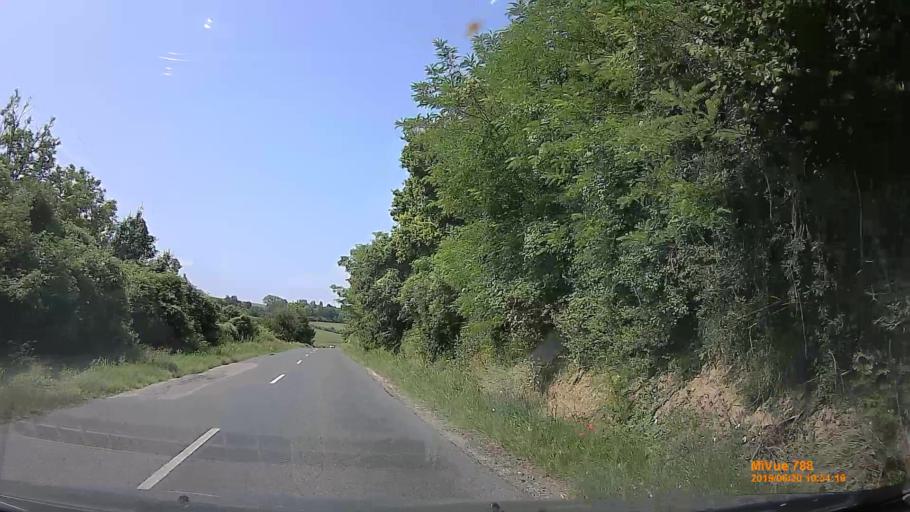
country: HU
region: Baranya
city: Mecseknadasd
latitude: 46.1554
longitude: 18.5656
